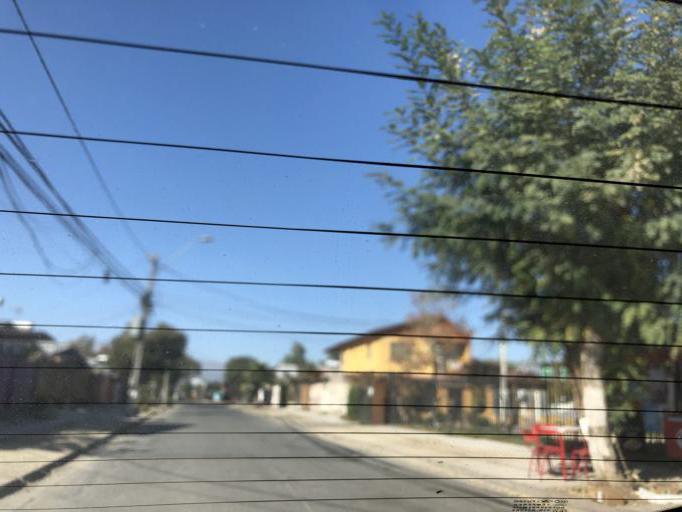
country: CL
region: Santiago Metropolitan
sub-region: Provincia de Cordillera
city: Puente Alto
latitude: -33.6279
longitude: -70.5915
